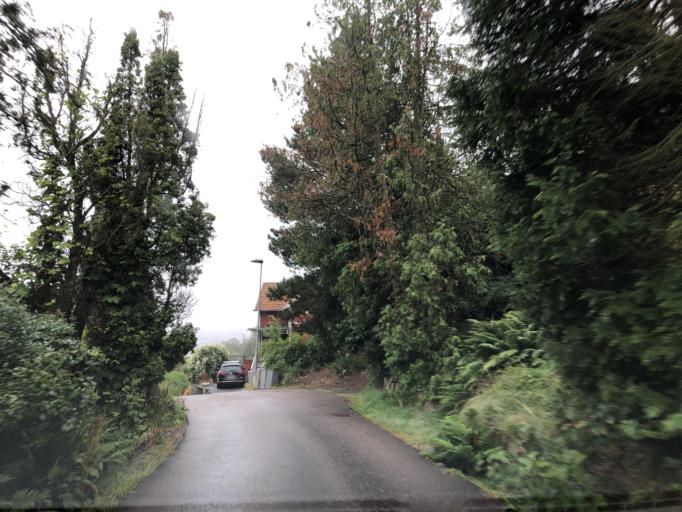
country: SE
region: Vaestra Goetaland
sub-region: Goteborg
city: Goeteborg
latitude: 57.7374
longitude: 11.9358
